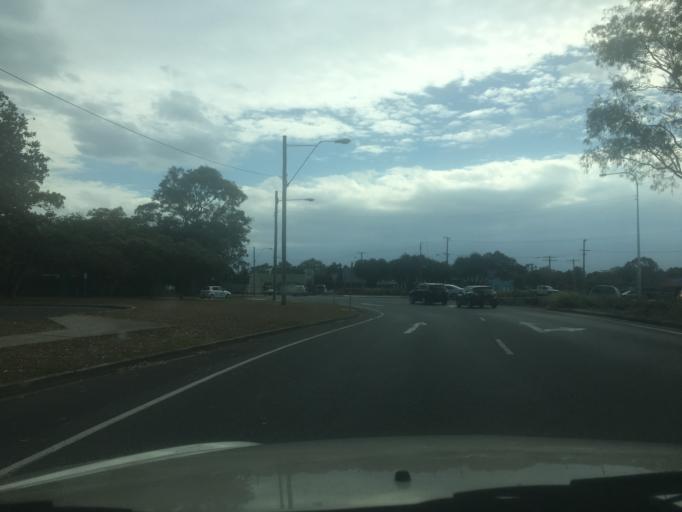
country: AU
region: Queensland
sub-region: Moreton Bay
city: Bongaree
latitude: -27.0663
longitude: 153.1505
